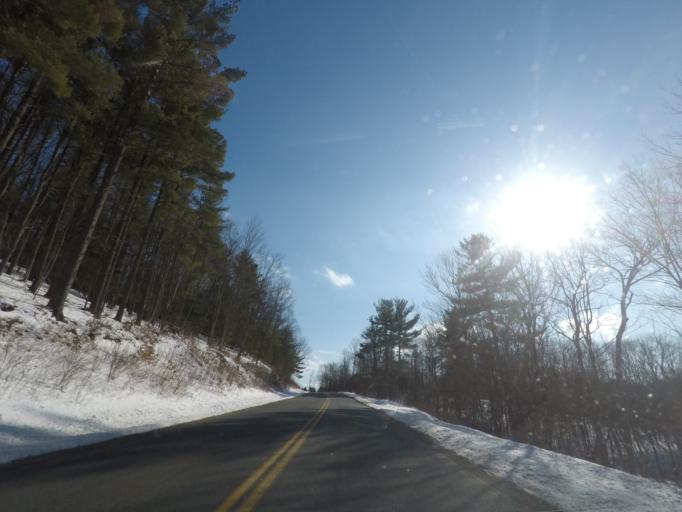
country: US
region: New York
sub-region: Rensselaer County
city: Hoosick Falls
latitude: 42.8887
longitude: -73.4959
